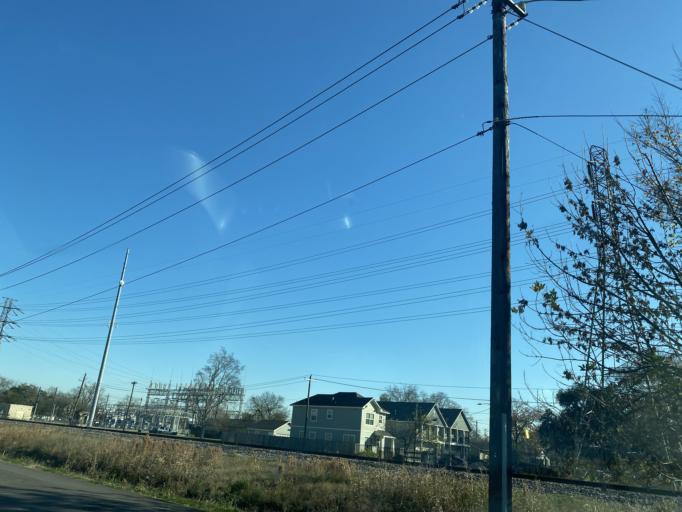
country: US
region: Texas
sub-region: Harris County
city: Houston
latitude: 29.8195
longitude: -95.3910
